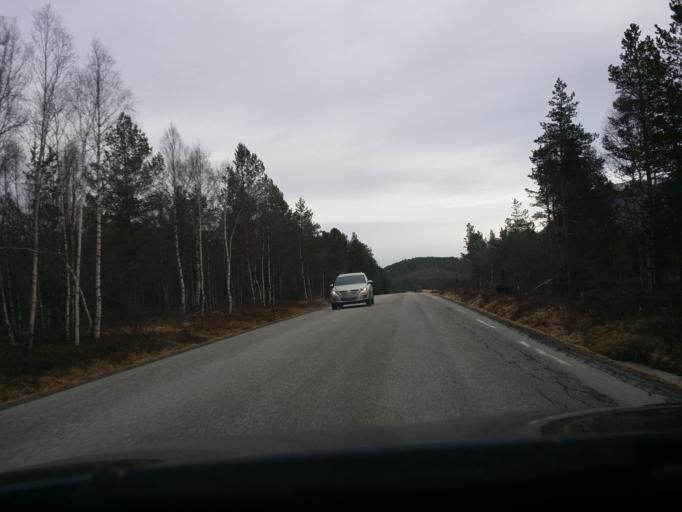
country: NO
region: More og Romsdal
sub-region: Halsa
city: Liaboen
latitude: 63.1242
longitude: 8.3512
